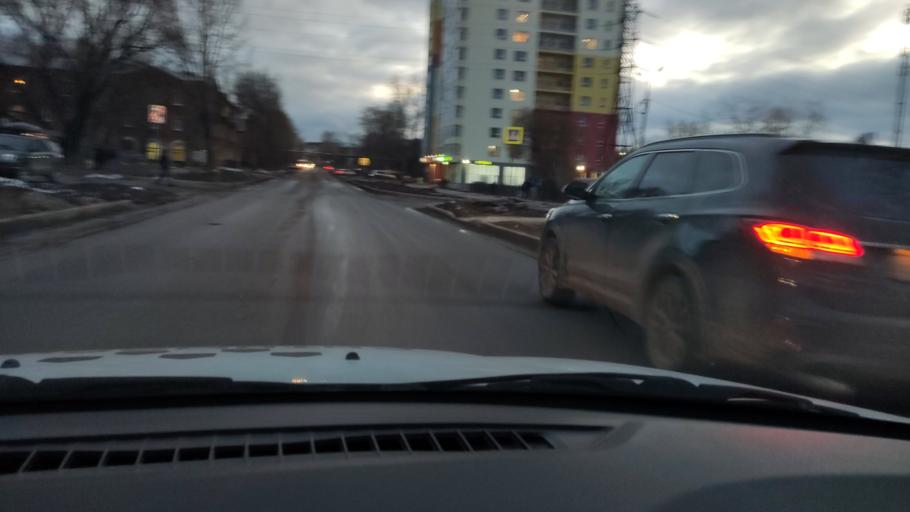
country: RU
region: Perm
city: Perm
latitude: 57.9724
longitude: 56.2751
